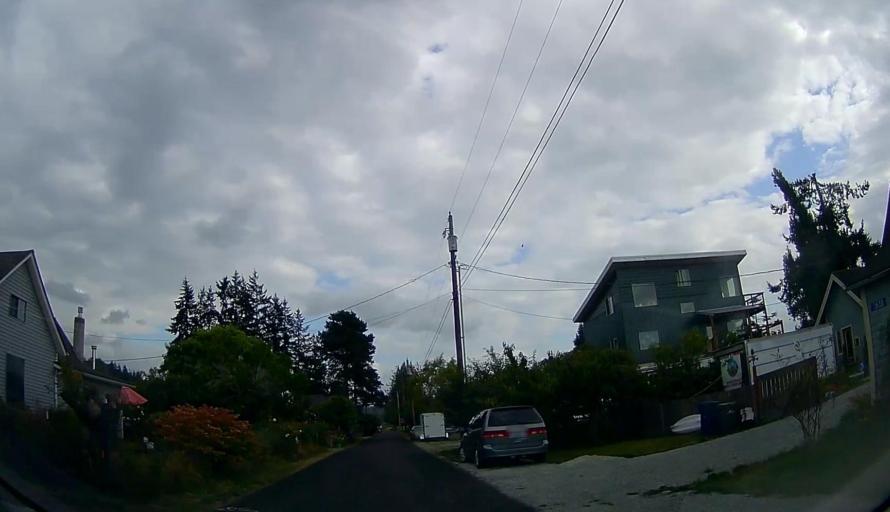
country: US
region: Washington
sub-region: Whatcom County
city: Sudden Valley
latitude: 48.5932
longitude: -122.4177
